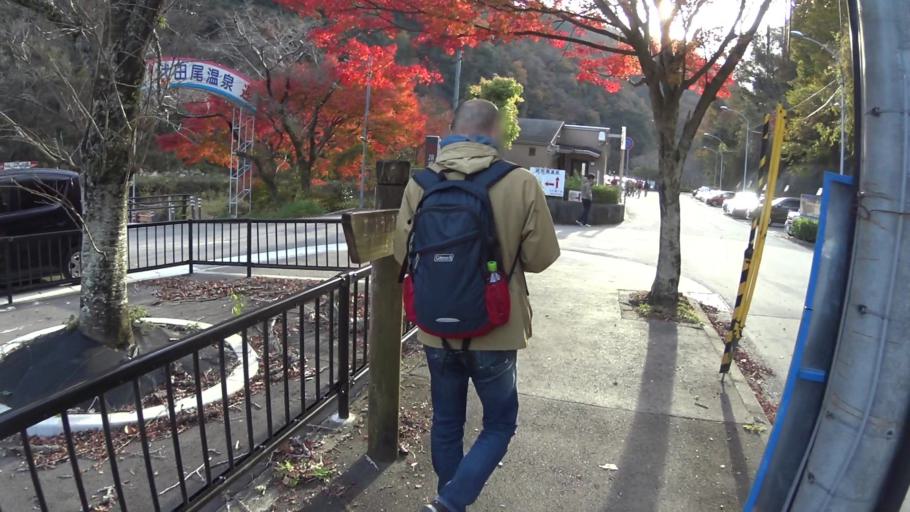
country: JP
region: Hyogo
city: Takarazuka
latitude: 34.8568
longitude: 135.3093
